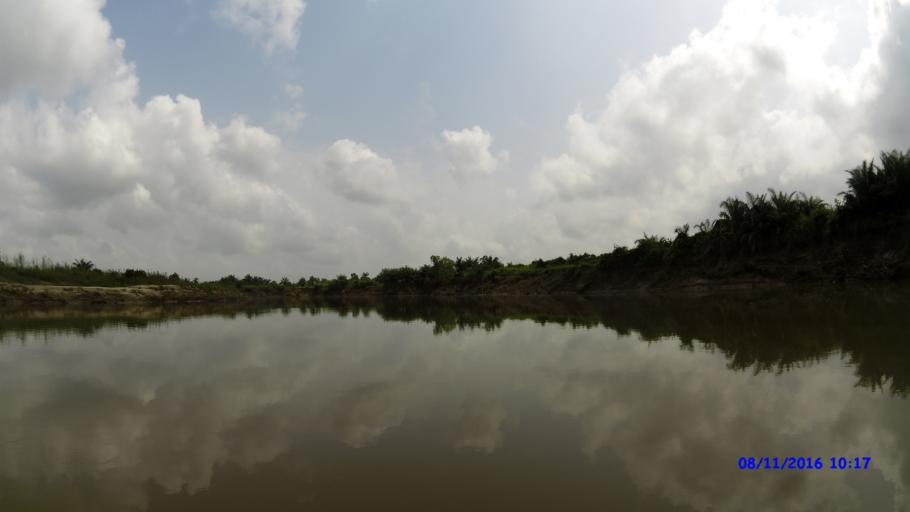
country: BJ
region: Mono
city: Come
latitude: 6.4579
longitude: 1.7568
